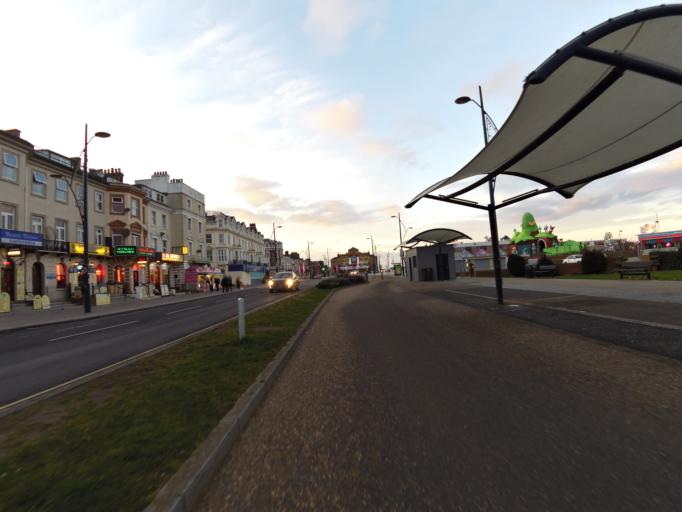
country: GB
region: England
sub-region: Norfolk
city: Great Yarmouth
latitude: 52.6071
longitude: 1.7369
